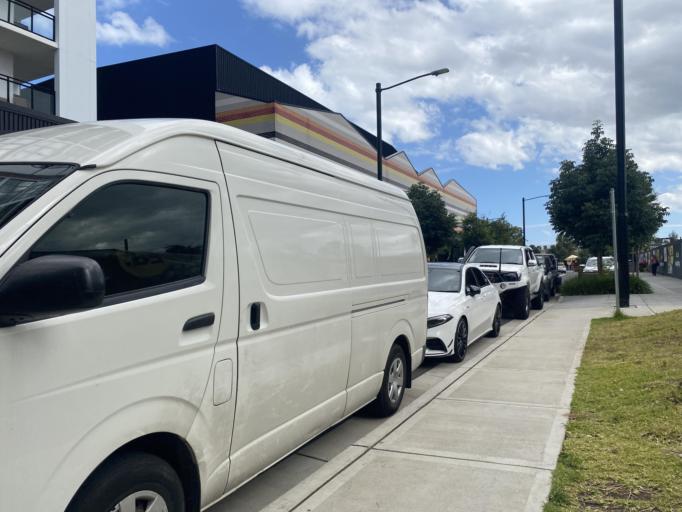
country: AU
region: New South Wales
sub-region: Campbelltown Municipality
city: Denham Court
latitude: -33.9701
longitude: 150.8579
